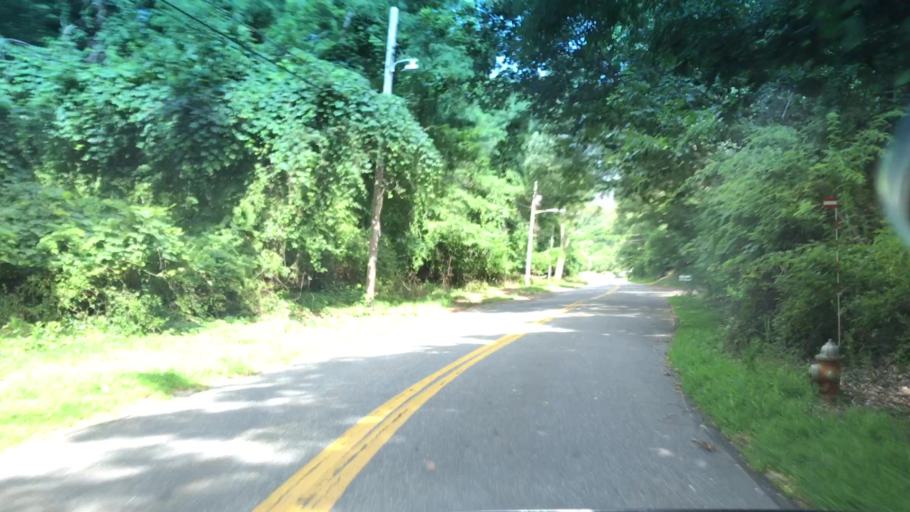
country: US
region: New York
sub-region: Suffolk County
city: Wading River
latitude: 40.9631
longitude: -72.8098
